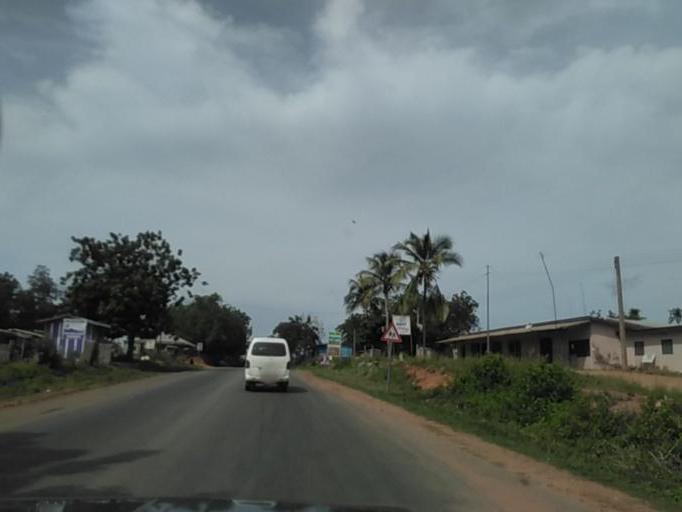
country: GH
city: Akropong
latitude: 6.2106
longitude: 0.0815
